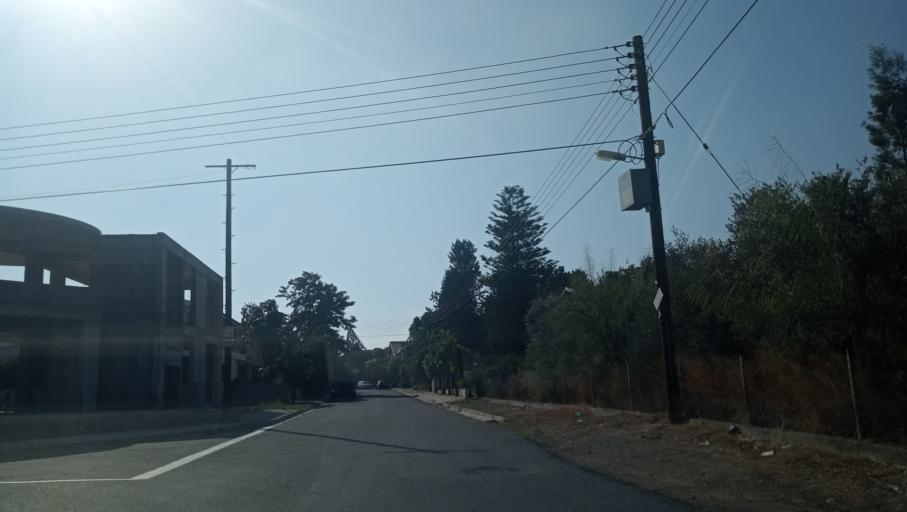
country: CY
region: Lefkosia
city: Nicosia
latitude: 35.1430
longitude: 33.3842
